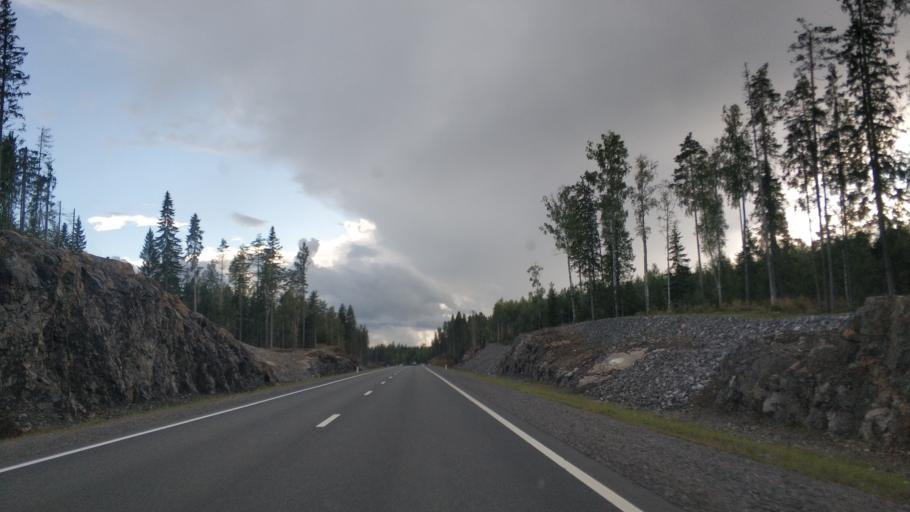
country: RU
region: Republic of Karelia
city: Lakhdenpokh'ya
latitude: 61.4323
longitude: 29.9741
